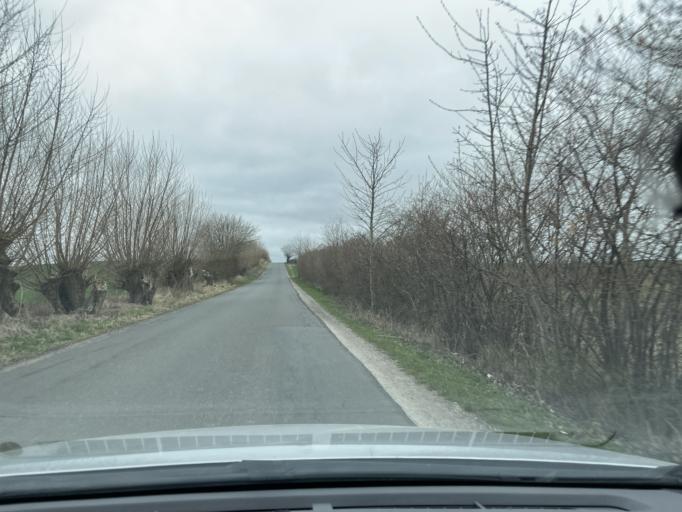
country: DK
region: South Denmark
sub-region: Nyborg Kommune
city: Nyborg
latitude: 55.3530
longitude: 10.7767
